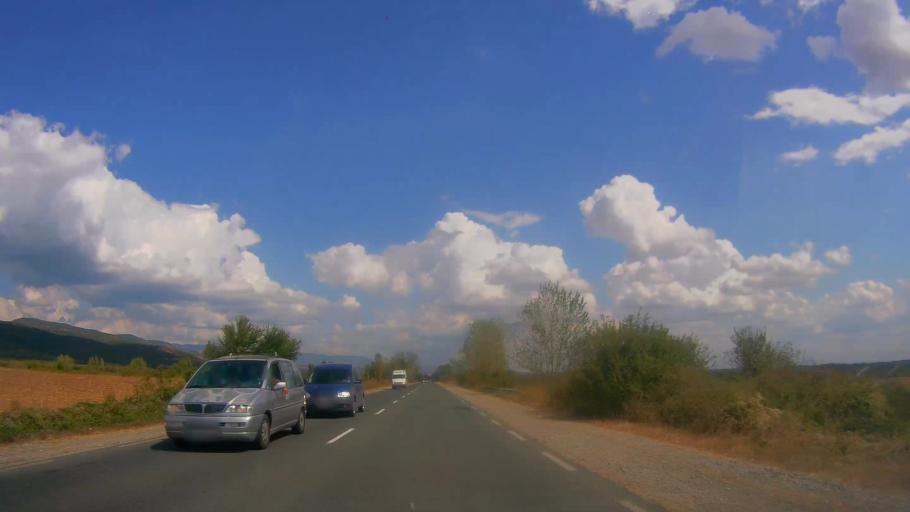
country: BG
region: Sliven
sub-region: Obshtina Sliven
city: Kermen
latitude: 42.6323
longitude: 26.1961
